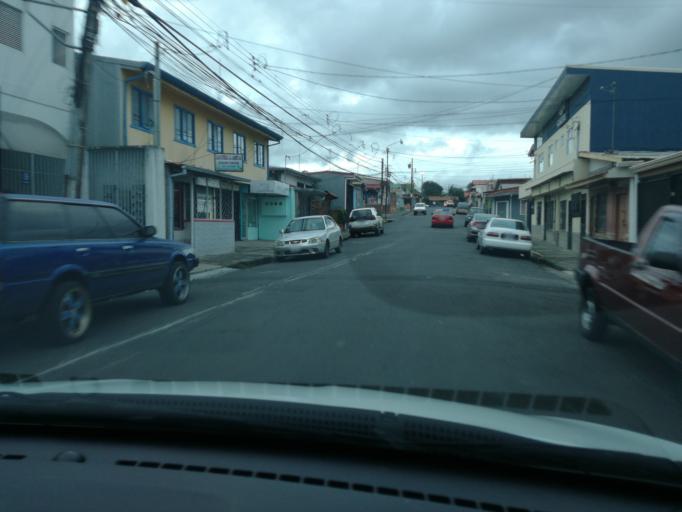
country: CR
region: San Jose
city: Sabanilla
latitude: 9.9368
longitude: -84.0377
